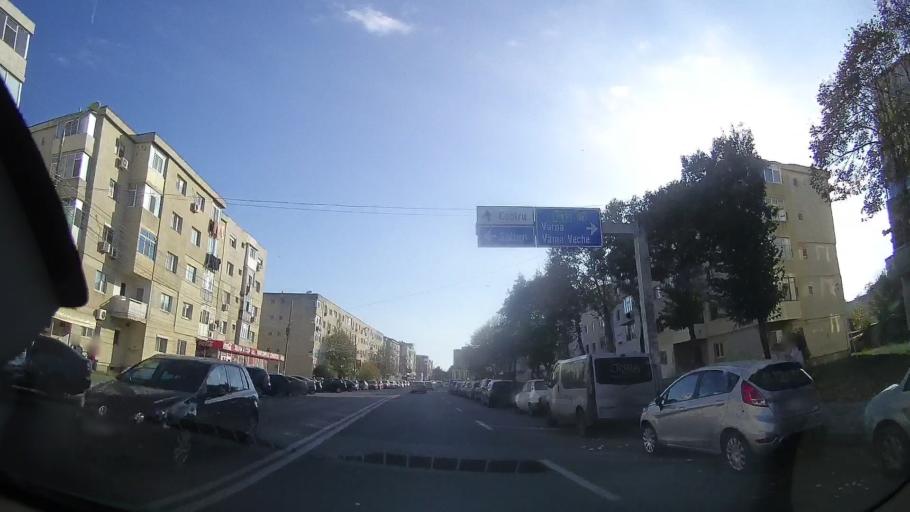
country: RO
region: Constanta
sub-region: Municipiul Mangalia
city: Mangalia
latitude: 43.8198
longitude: 28.5829
